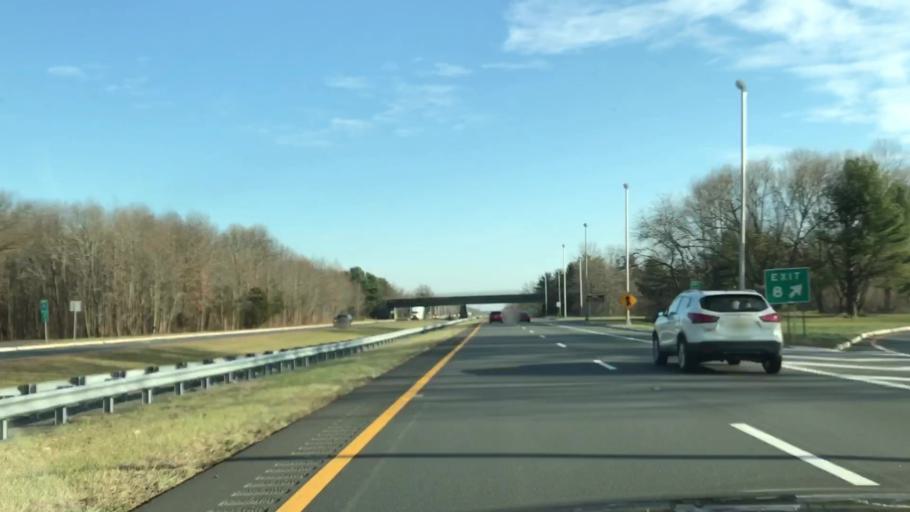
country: US
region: New Jersey
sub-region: Monmouth County
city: Allentown
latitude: 40.1869
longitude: -74.5737
